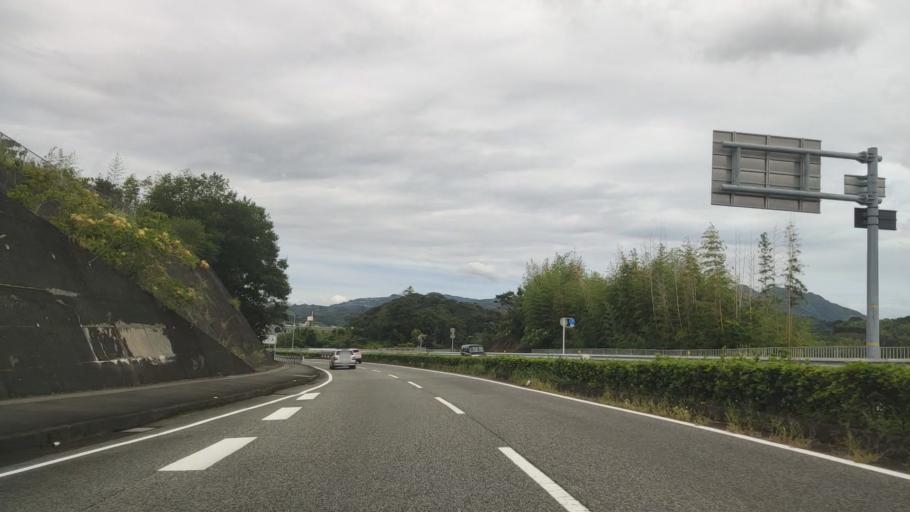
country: JP
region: Wakayama
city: Tanabe
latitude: 33.7346
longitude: 135.4005
